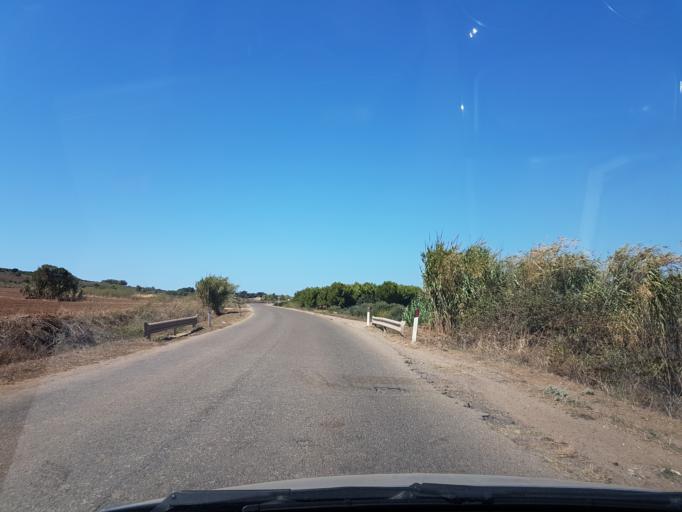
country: IT
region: Sardinia
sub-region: Provincia di Oristano
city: Cabras
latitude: 39.9509
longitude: 8.4554
